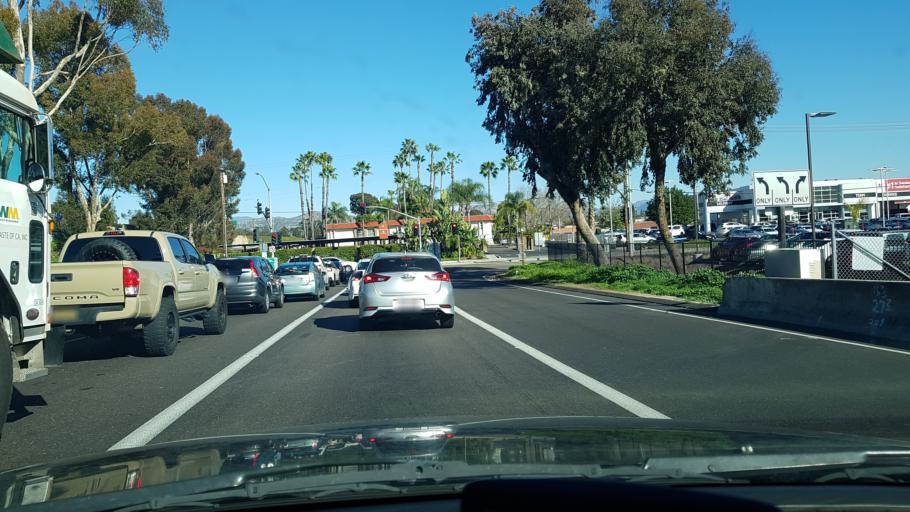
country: US
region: California
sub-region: San Diego County
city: El Cajon
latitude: 32.8023
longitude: -116.9719
